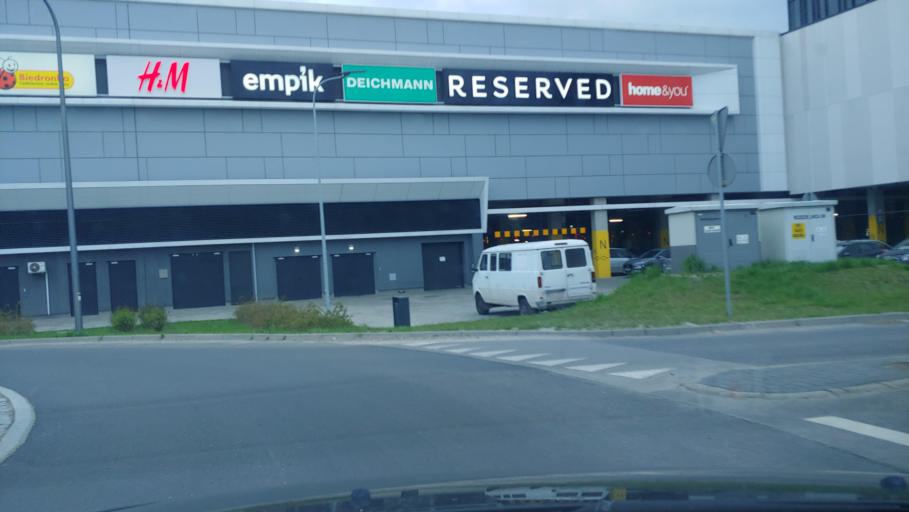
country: PL
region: Silesian Voivodeship
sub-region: Tychy
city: Cielmice
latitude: 50.0972
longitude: 19.0105
